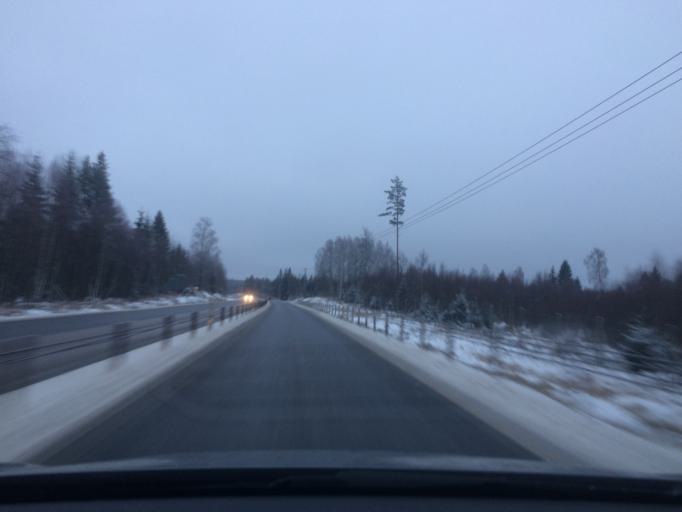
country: SE
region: Kronoberg
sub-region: Vaxjo Kommun
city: Vaexjoe
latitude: 56.8785
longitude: 14.9017
